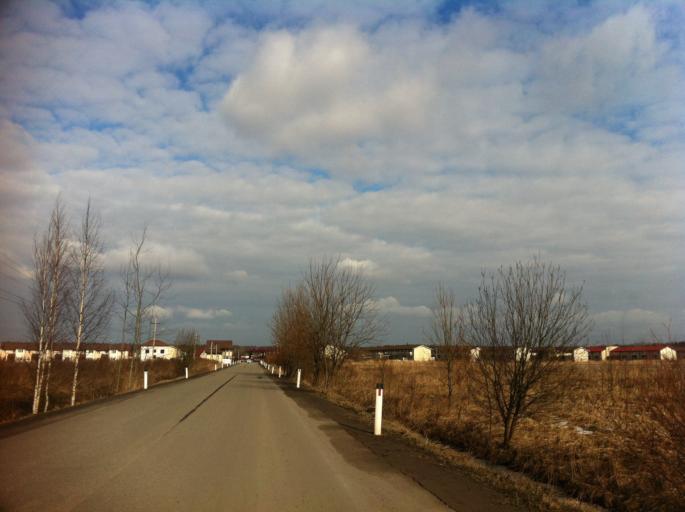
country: RU
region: Leningrad
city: Yanino Vtoroye
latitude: 59.9585
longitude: 30.5702
